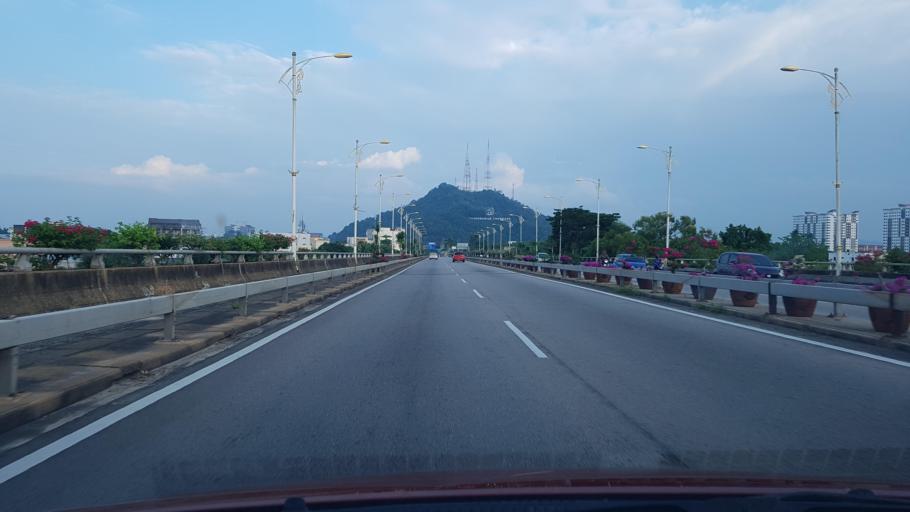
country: MY
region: Terengganu
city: Kuala Terengganu
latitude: 5.3207
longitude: 103.1268
